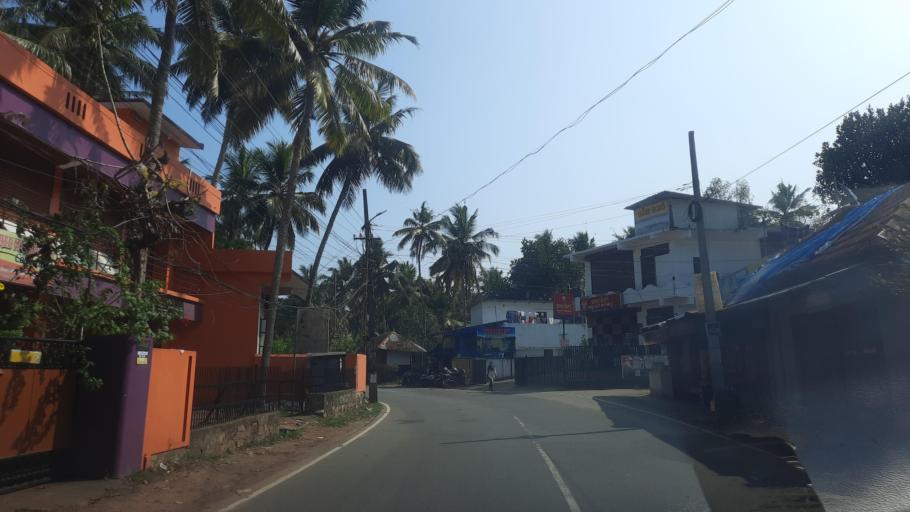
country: IN
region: Kerala
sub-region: Thiruvananthapuram
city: Nedumangad
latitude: 8.5753
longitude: 76.9253
